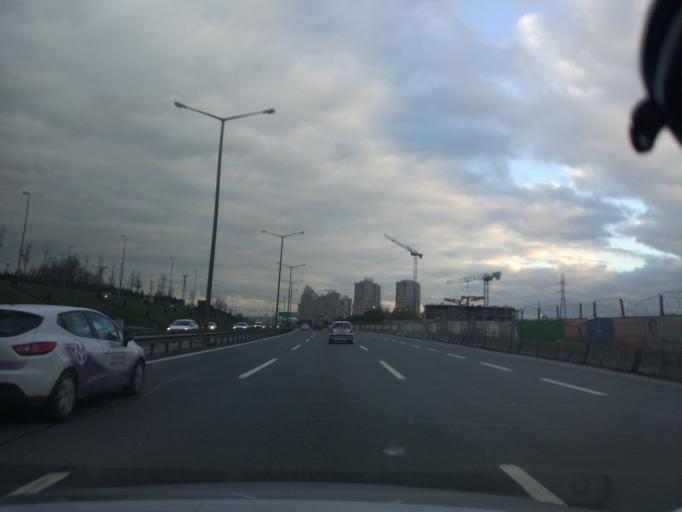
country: TR
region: Istanbul
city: Esenler
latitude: 41.0724
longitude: 28.8677
